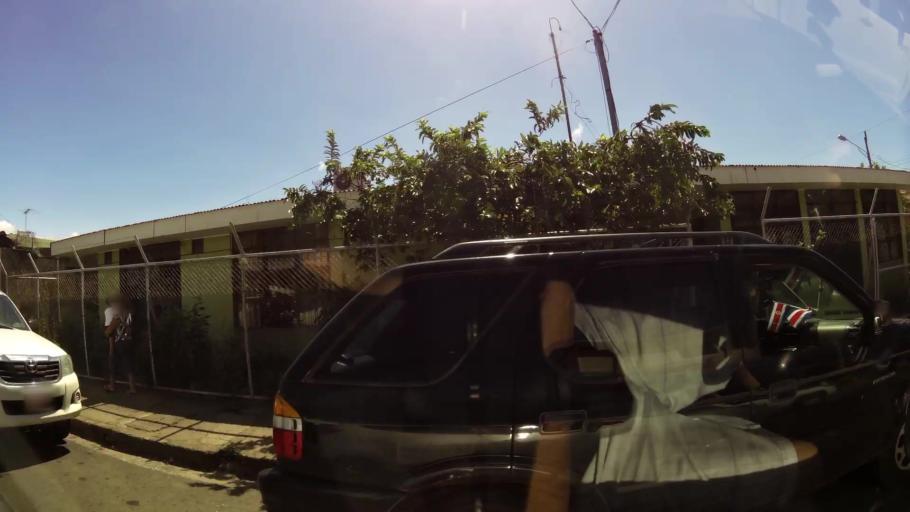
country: CR
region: Guanacaste
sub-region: Canton de Canas
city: Canas
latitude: 10.4263
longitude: -85.0927
